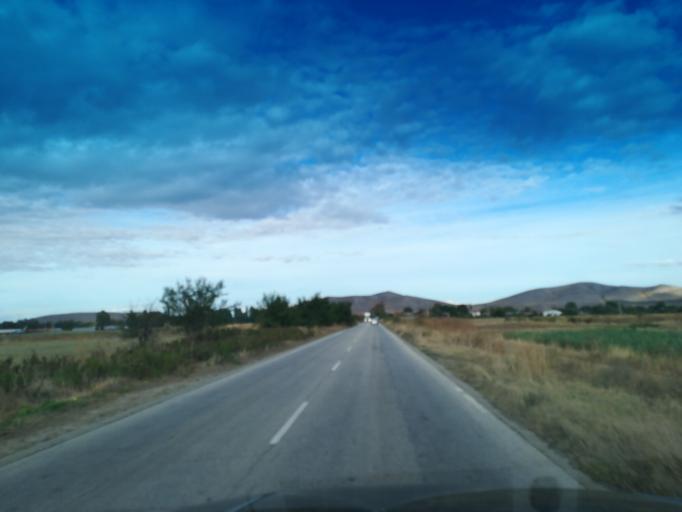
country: BG
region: Plovdiv
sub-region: Obshtina Krichim
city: Krichim
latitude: 42.0791
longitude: 24.4174
